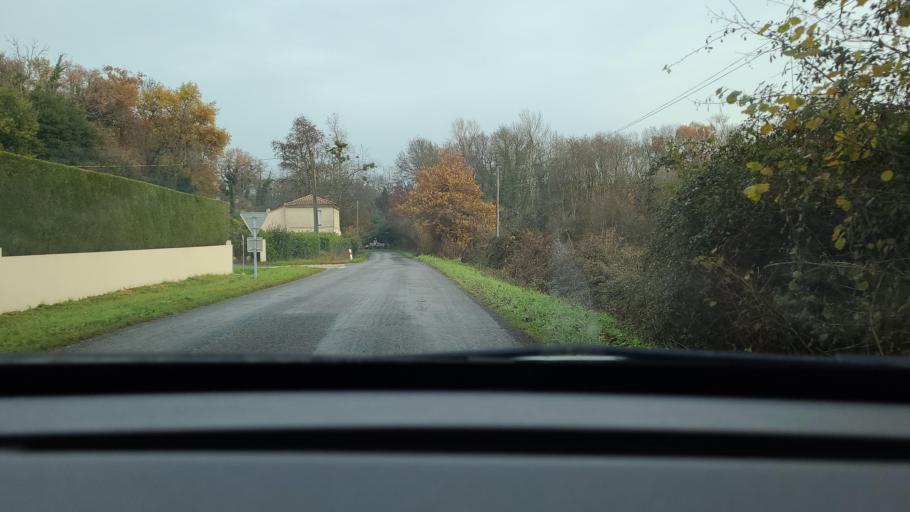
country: FR
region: Aquitaine
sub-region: Departement de la Gironde
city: Tauriac
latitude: 45.0385
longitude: -0.5077
